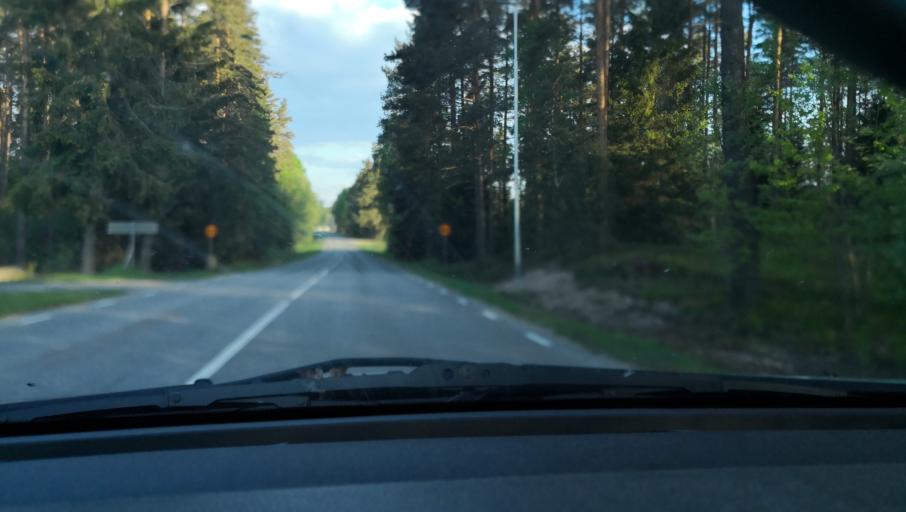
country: SE
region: Joenkoeping
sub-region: Vetlanda Kommun
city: Landsbro
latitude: 57.3758
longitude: 14.8783
